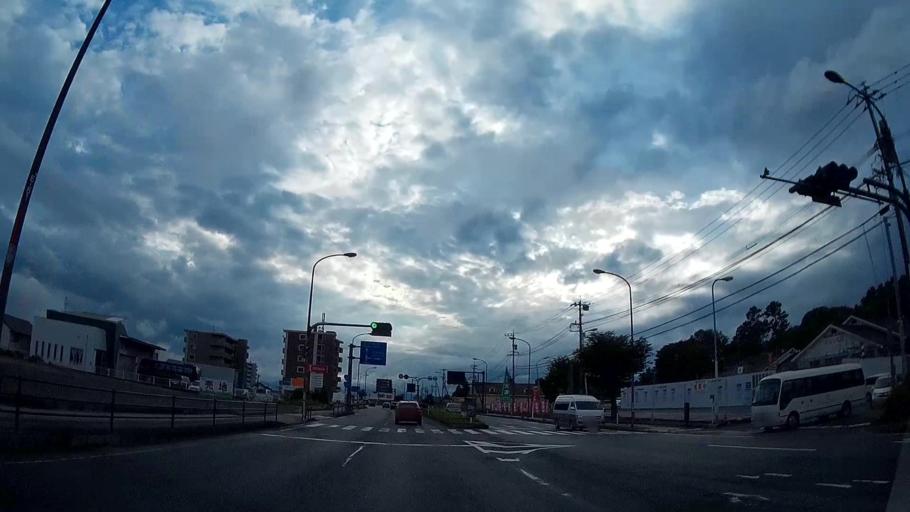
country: JP
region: Kumamoto
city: Ozu
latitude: 32.8803
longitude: 130.8918
